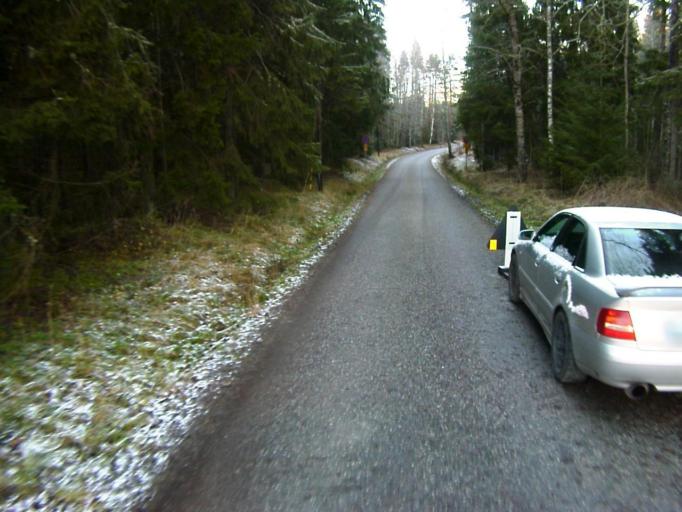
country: SE
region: Soedermanland
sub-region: Eskilstuna Kommun
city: Arla
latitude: 59.3228
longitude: 16.5969
